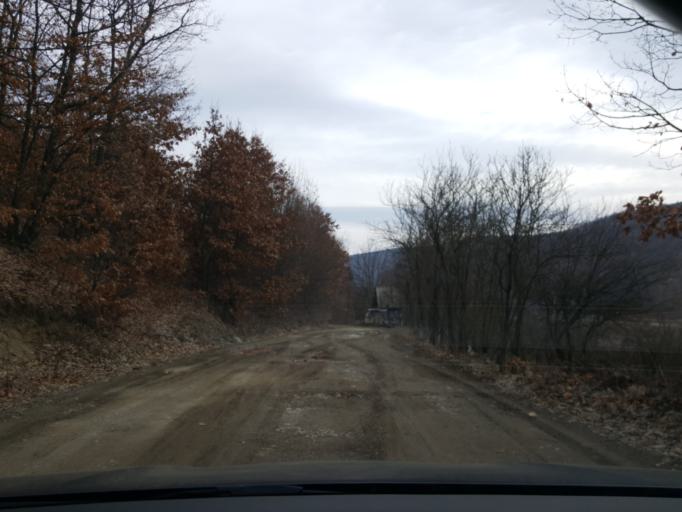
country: RS
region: Central Serbia
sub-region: Pirotski Okrug
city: Dimitrovgrad
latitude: 42.9977
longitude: 22.7479
